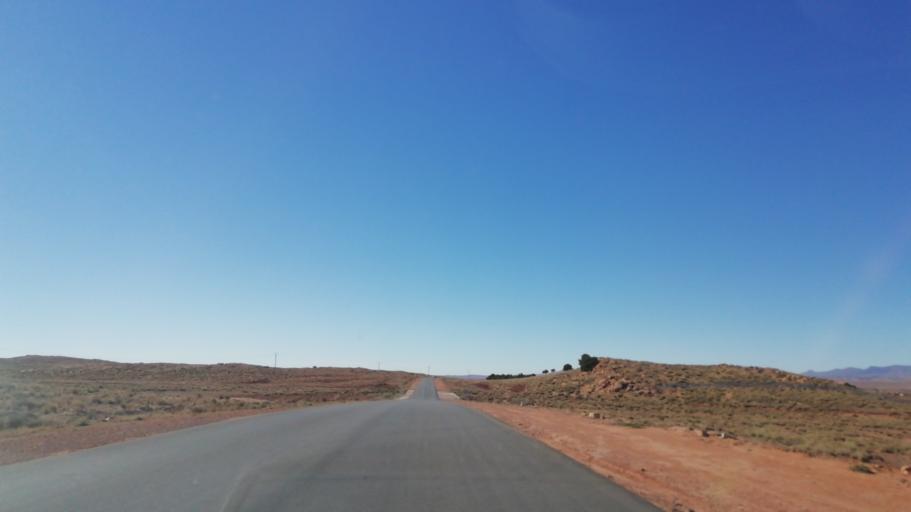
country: DZ
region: El Bayadh
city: El Bayadh
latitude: 33.6374
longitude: 1.3807
